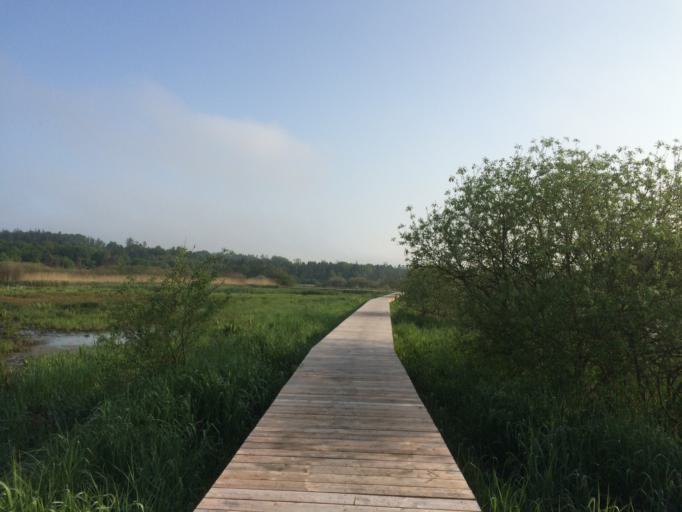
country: DK
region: Central Jutland
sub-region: Silkeborg Kommune
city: Svejbaek
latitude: 56.1988
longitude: 9.6496
